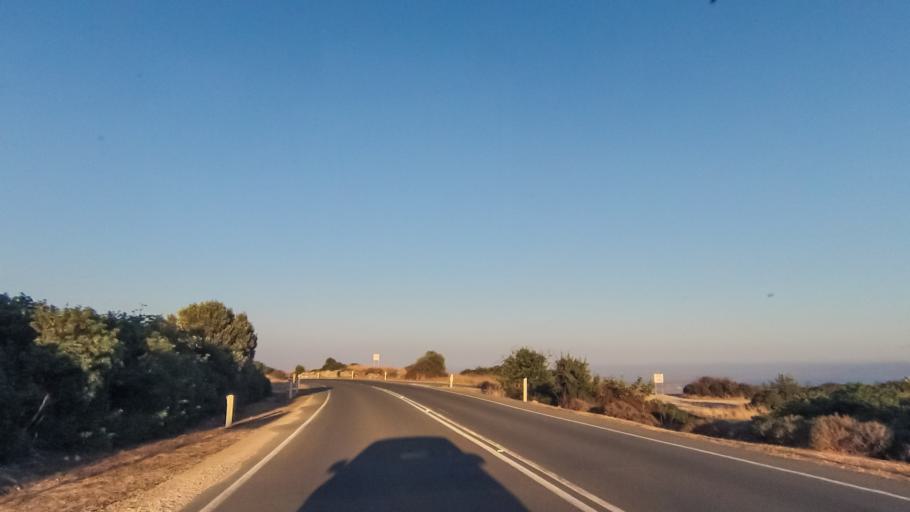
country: CY
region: Limassol
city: Erimi
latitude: 34.6699
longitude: 32.8769
